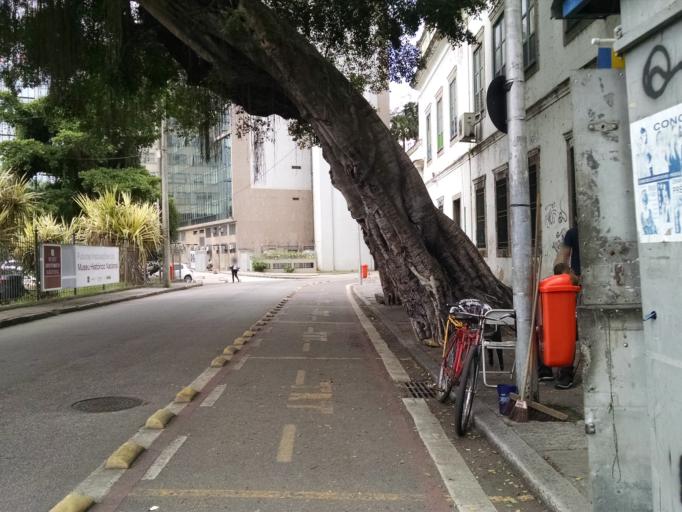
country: BR
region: Rio de Janeiro
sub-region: Rio De Janeiro
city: Rio de Janeiro
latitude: -22.9066
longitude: -43.1697
